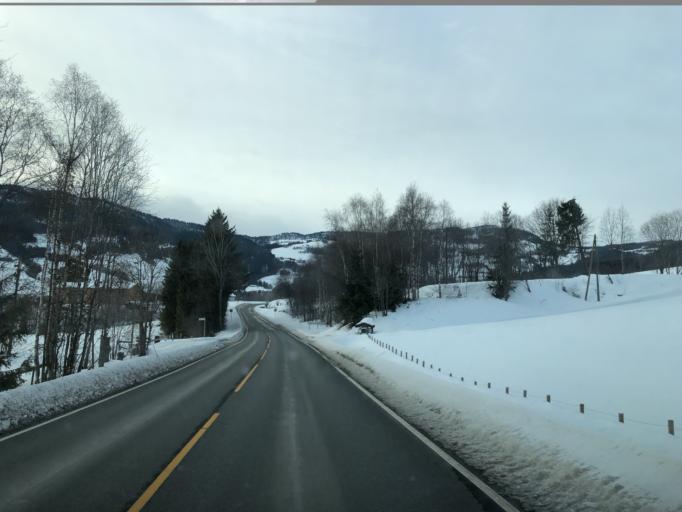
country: NO
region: Oppland
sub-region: Gausdal
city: Segalstad bru
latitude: 61.2603
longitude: 10.1645
